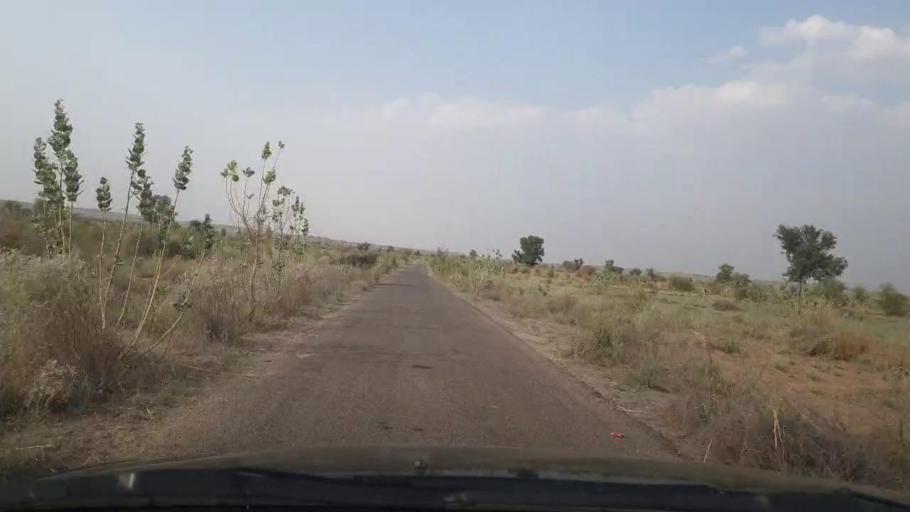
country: PK
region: Sindh
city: Islamkot
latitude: 25.0561
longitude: 70.5601
